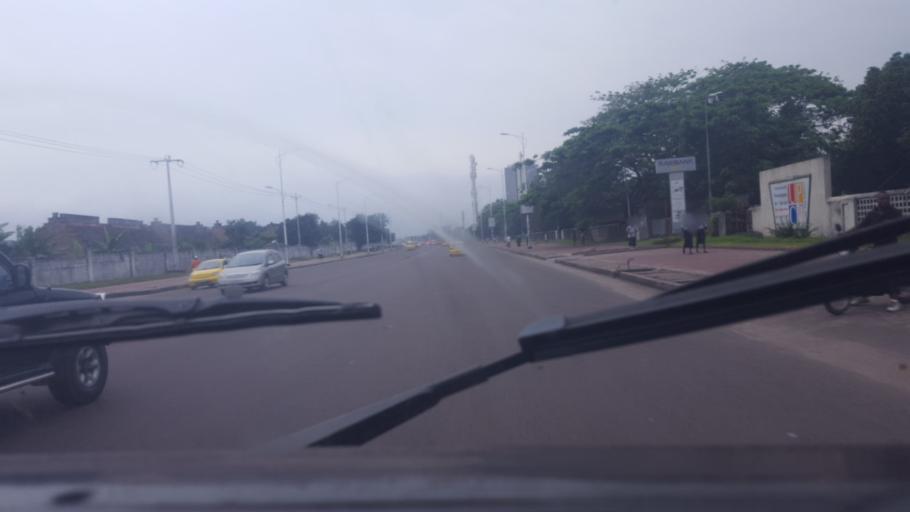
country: CD
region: Kinshasa
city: Kinshasa
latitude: -4.3358
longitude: 15.2966
